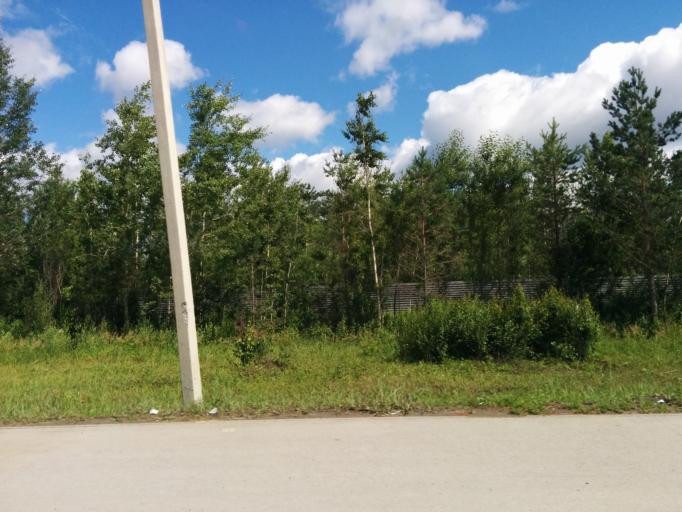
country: RU
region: Perm
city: Perm
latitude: 58.0327
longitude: 56.2082
